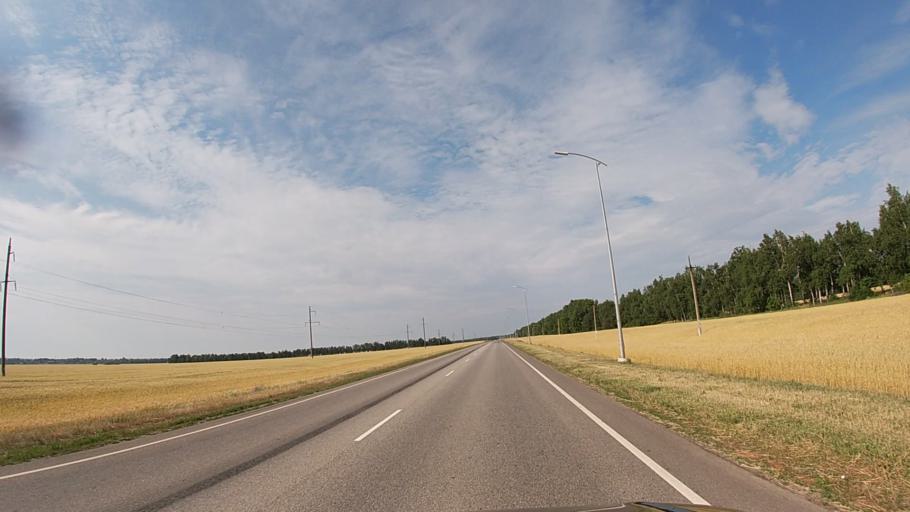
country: RU
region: Belgorod
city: Proletarskiy
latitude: 50.8192
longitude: 35.7554
